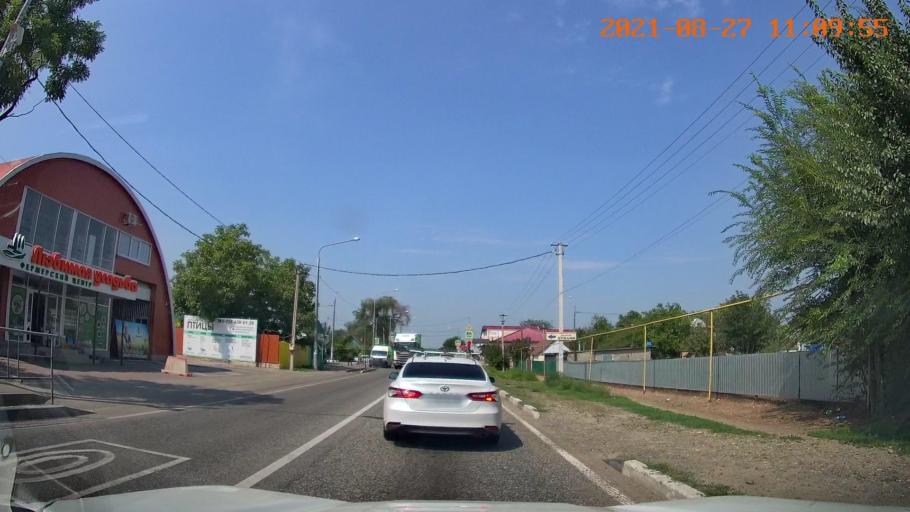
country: RU
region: Stavropol'skiy
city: Ivanovskoye
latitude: 44.5714
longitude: 41.8725
